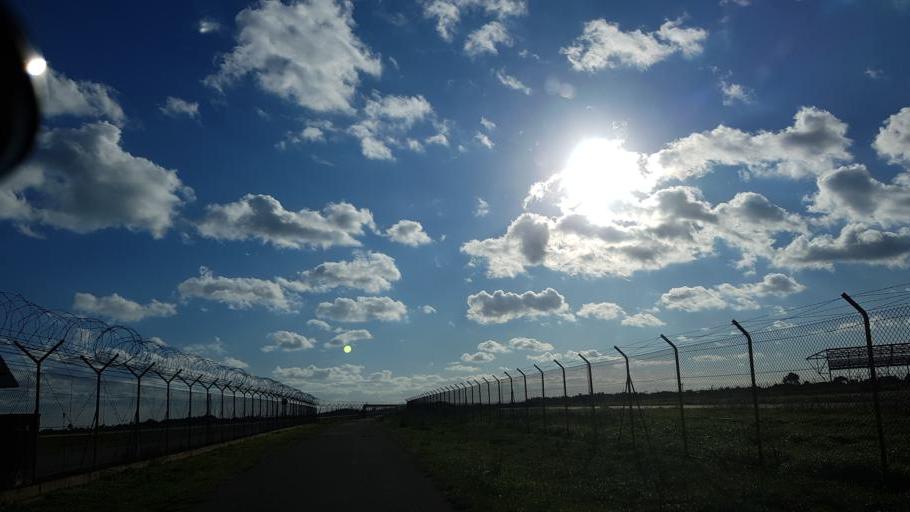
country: IT
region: Apulia
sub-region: Provincia di Brindisi
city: Materdomini
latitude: 40.6742
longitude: 17.9241
